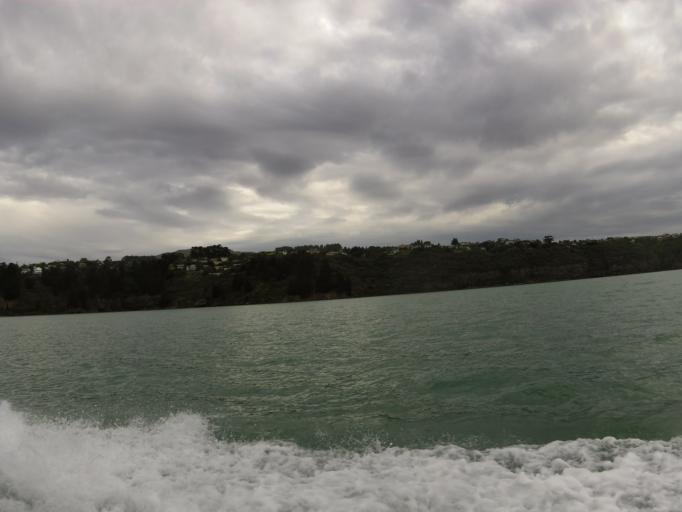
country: NZ
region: Canterbury
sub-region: Christchurch City
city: Christchurch
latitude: -43.6209
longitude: 172.7321
